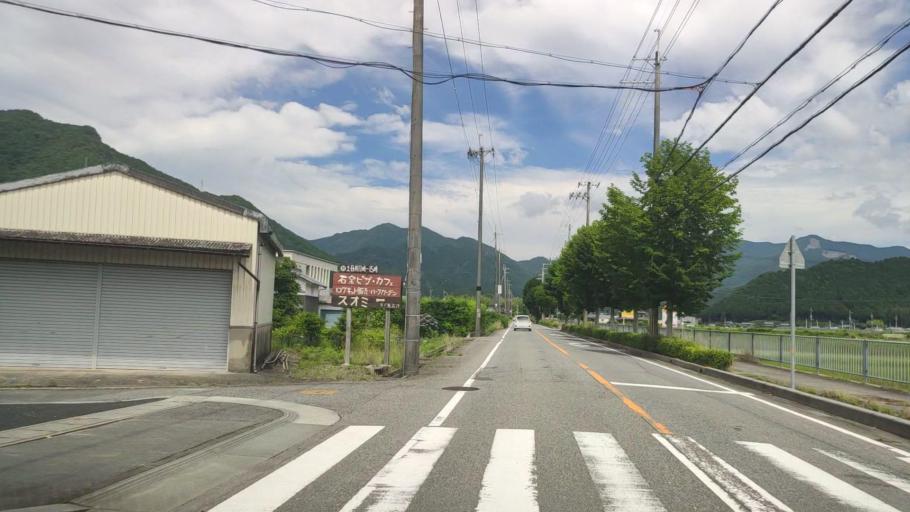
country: JP
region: Hyogo
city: Nishiwaki
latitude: 35.0721
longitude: 134.9035
